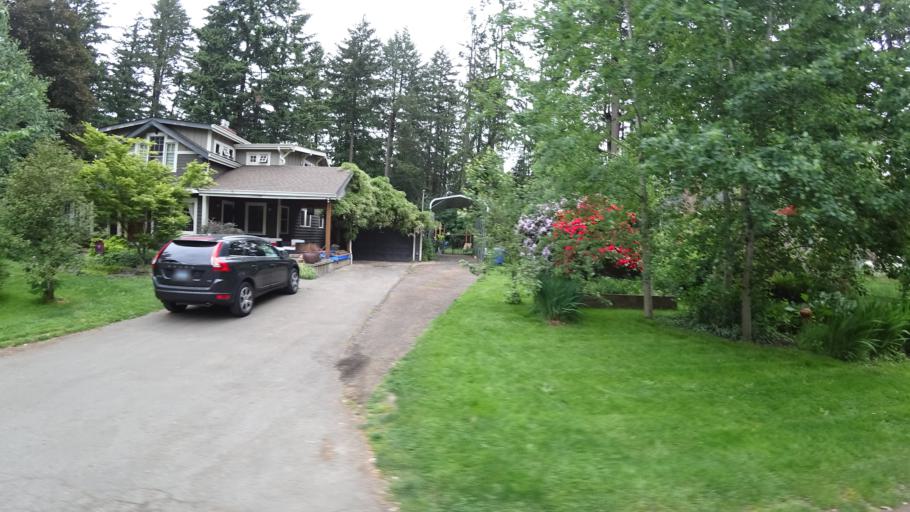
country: US
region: Oregon
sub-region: Washington County
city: Garden Home-Whitford
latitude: 45.4625
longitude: -122.7343
